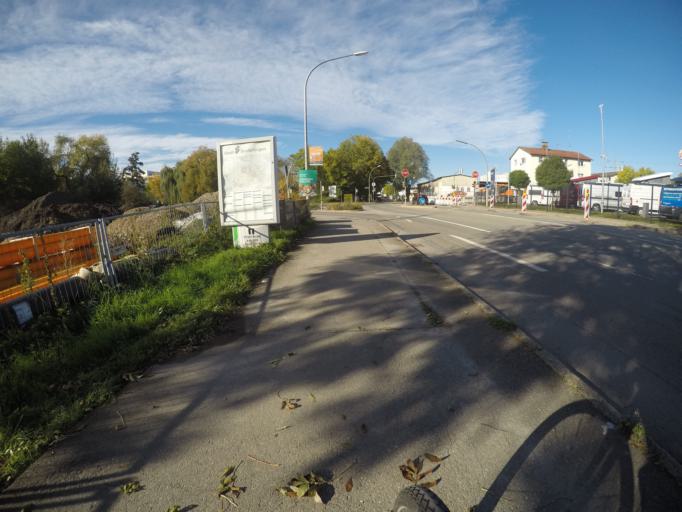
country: DE
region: Baden-Wuerttemberg
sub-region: Regierungsbezirk Stuttgart
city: Sindelfingen
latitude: 48.7053
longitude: 9.0272
